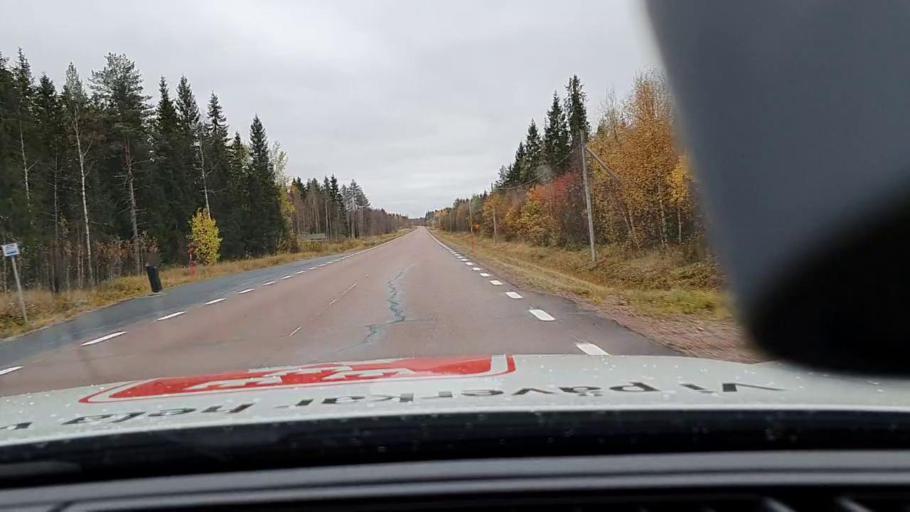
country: FI
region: Lapland
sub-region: Kemi-Tornio
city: Tornio
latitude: 66.0867
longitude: 23.9251
